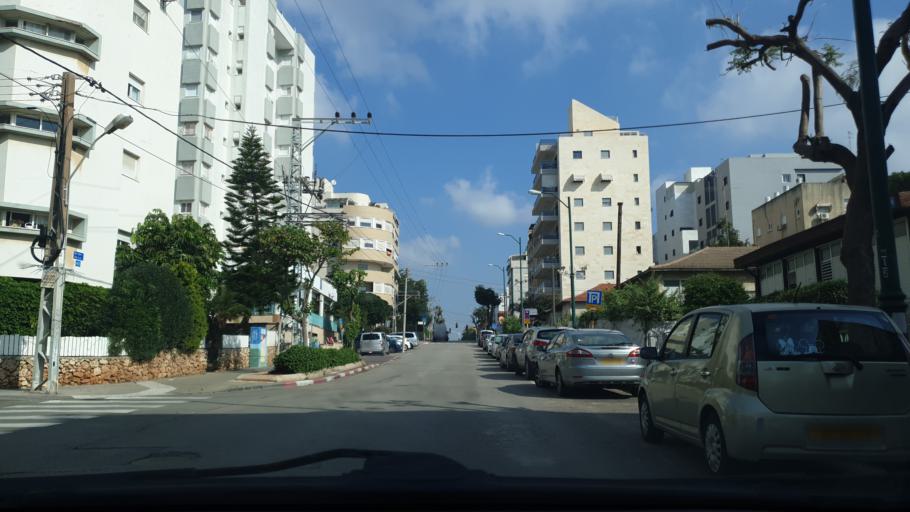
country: IL
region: Central District
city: Rishon LeZiyyon
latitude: 31.9671
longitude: 34.8115
